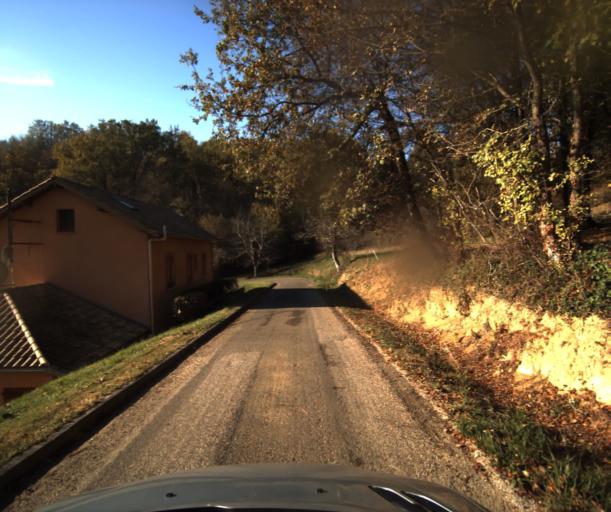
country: FR
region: Midi-Pyrenees
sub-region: Departement du Tarn-et-Garonne
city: Lafrancaise
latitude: 44.1068
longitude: 1.2915
